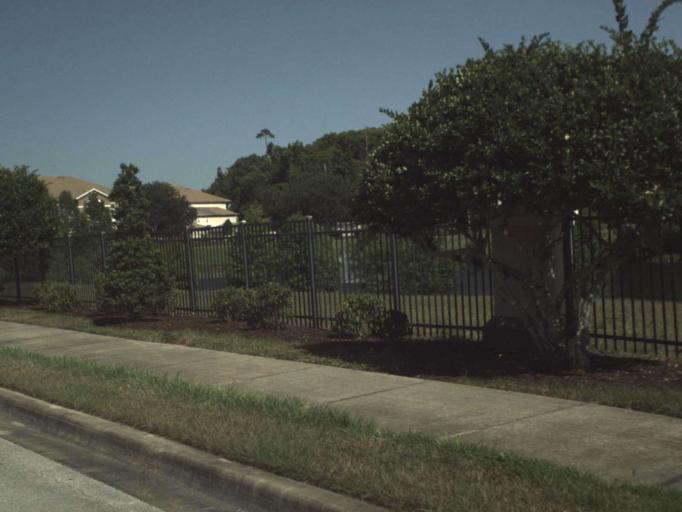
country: US
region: Florida
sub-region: Seminole County
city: Oviedo
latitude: 28.6899
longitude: -81.2401
